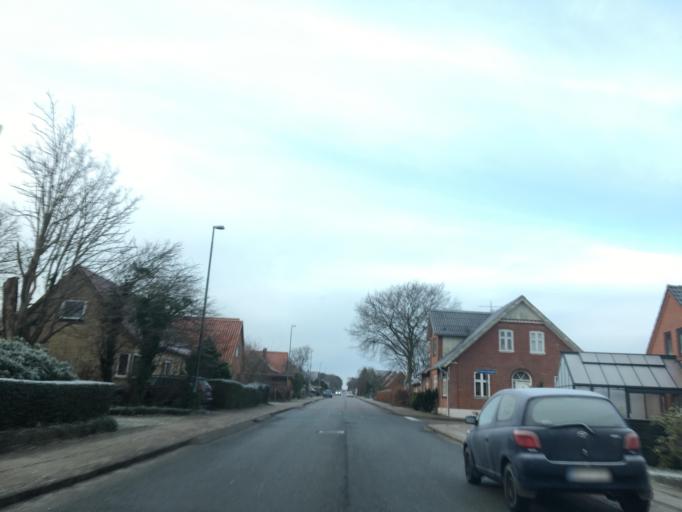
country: DK
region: North Denmark
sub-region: Thisted Kommune
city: Hurup
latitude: 56.7509
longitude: 8.4120
